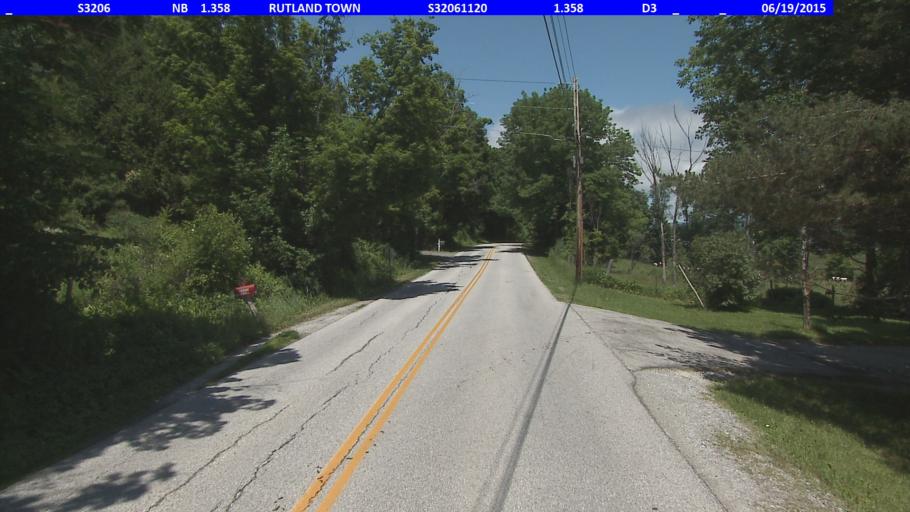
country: US
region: Vermont
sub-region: Rutland County
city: Rutland
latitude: 43.6482
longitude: -72.9961
